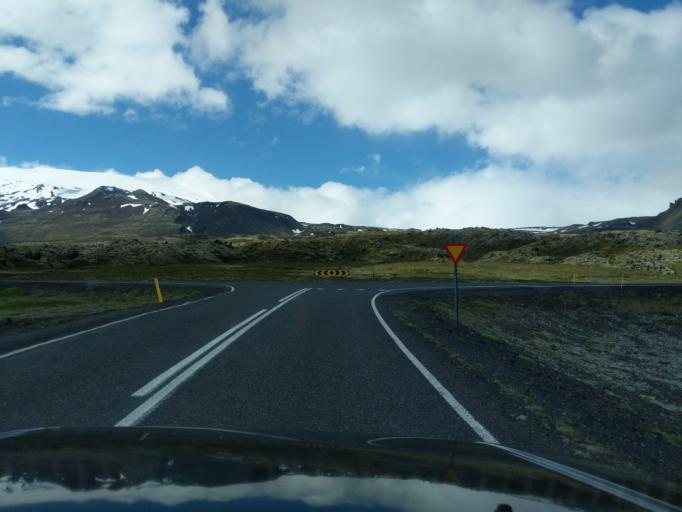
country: IS
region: West
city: Olafsvik
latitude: 64.7619
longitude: -23.6770
